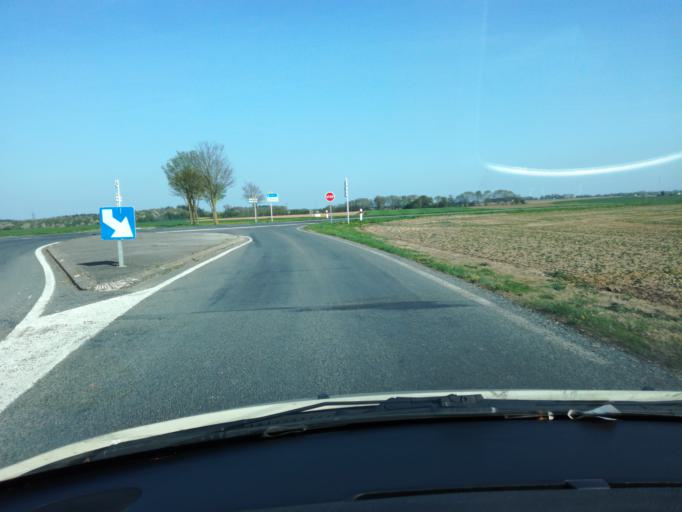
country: FR
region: Picardie
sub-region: Departement de la Somme
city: Poix-de-Picardie
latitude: 49.8218
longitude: 1.9552
